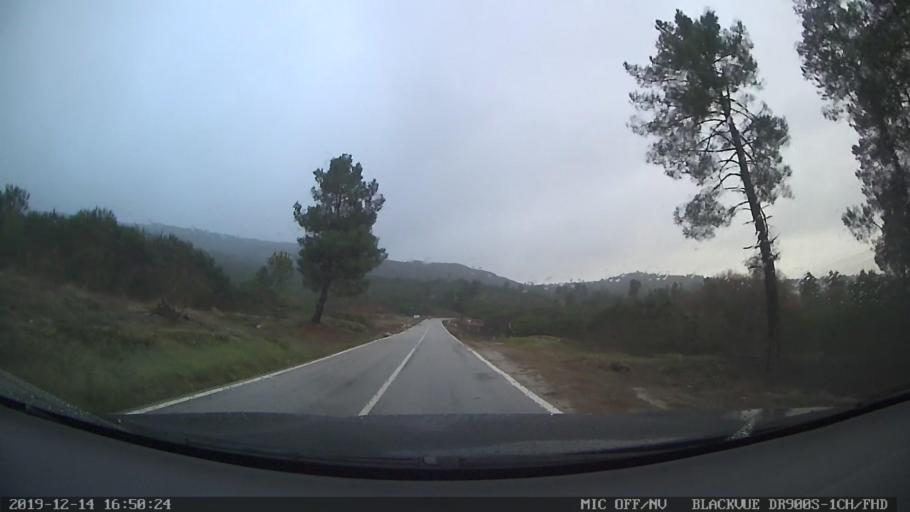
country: PT
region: Vila Real
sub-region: Murca
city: Murca
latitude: 41.4162
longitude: -7.5043
